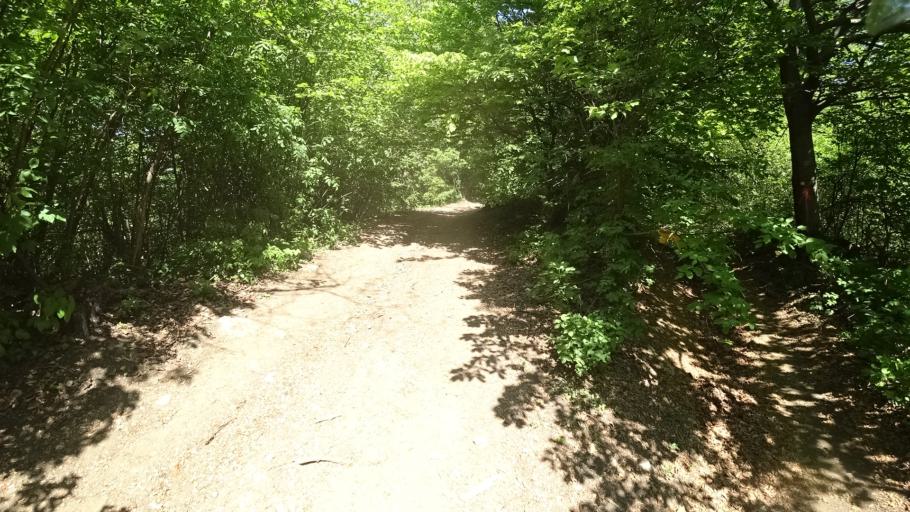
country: HR
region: Zagrebacka
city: Zapresic
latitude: 45.8383
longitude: 15.8386
